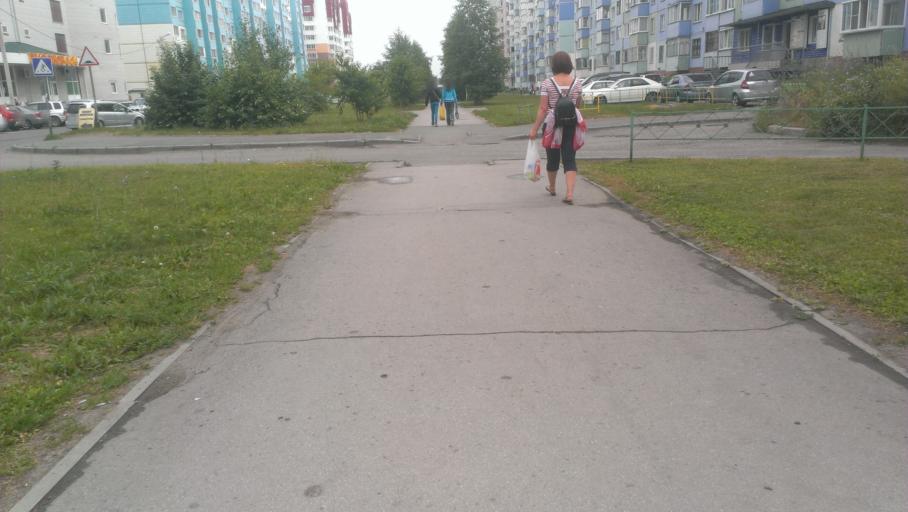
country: RU
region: Altai Krai
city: Novosilikatnyy
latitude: 53.3331
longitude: 83.6848
